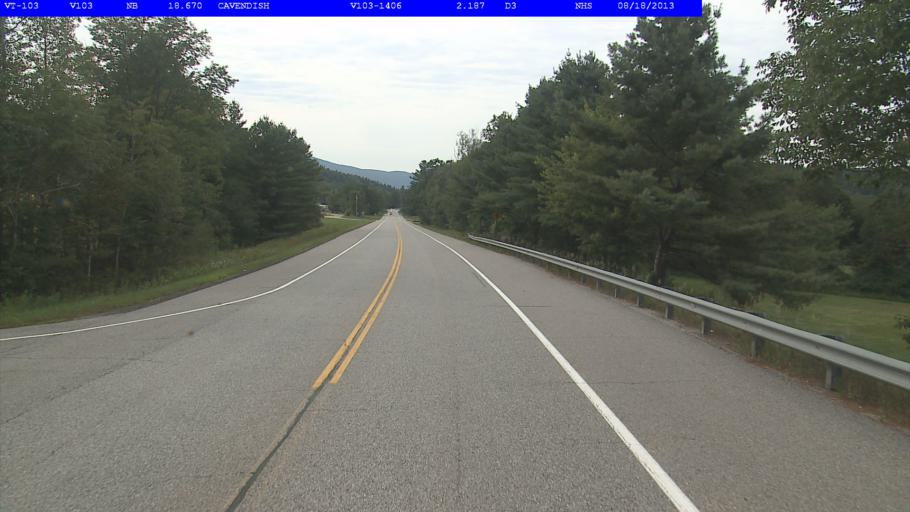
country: US
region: Vermont
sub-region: Windsor County
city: Chester
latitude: 43.3773
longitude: -72.6365
